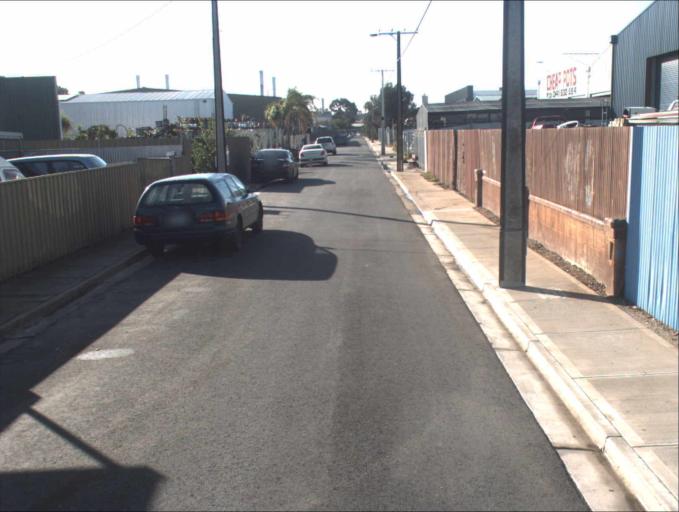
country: AU
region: South Australia
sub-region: Charles Sturt
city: Woodville North
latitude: -34.8466
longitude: 138.5468
